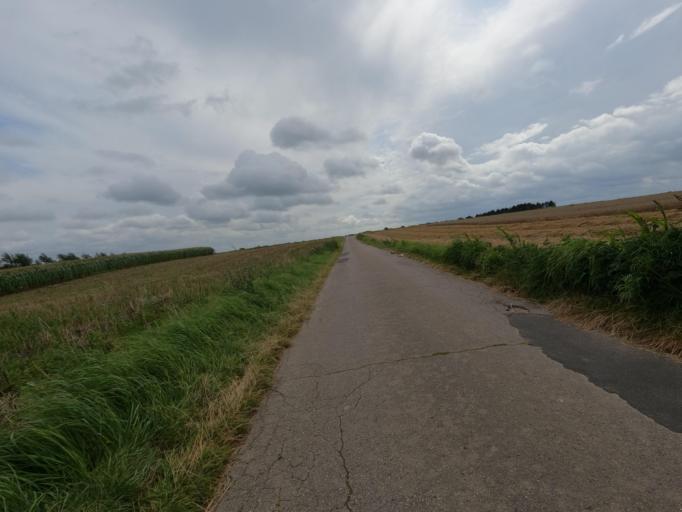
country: DE
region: North Rhine-Westphalia
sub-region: Regierungsbezirk Koln
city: Gangelt
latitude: 51.0108
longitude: 6.0123
